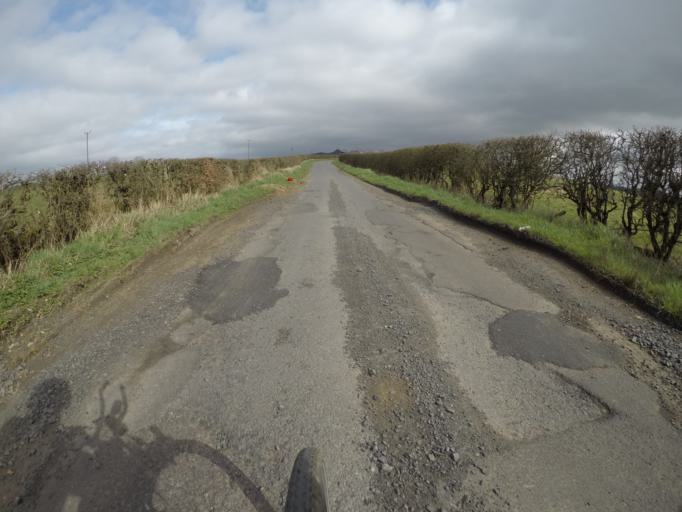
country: GB
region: Scotland
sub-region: North Ayrshire
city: Springside
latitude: 55.6675
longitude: -4.5880
